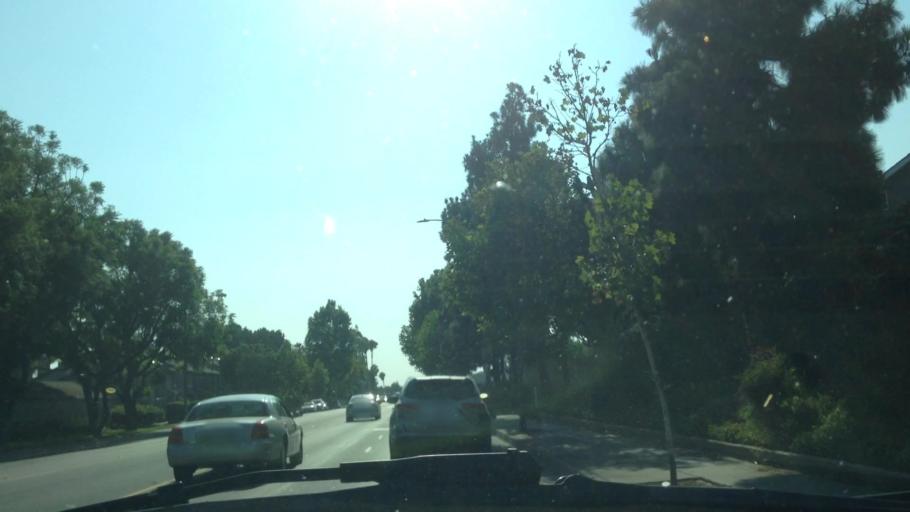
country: US
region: California
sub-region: Orange County
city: Placentia
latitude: 33.8743
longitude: -117.8907
